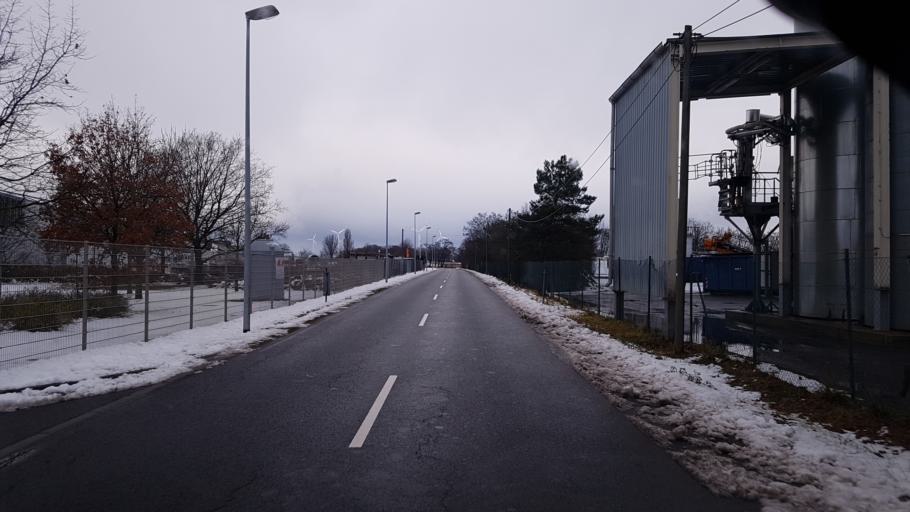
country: DE
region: Brandenburg
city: Luckau
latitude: 51.8780
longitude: 13.7966
